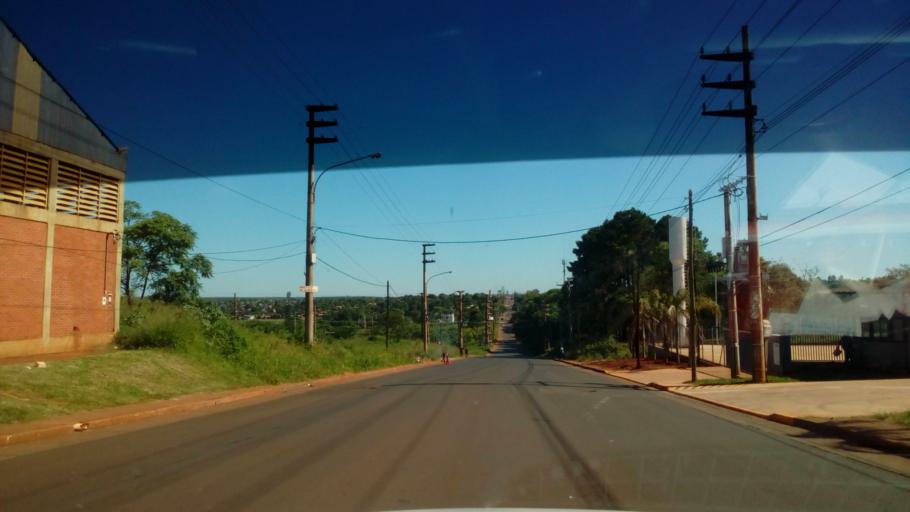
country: AR
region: Misiones
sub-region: Departamento de Capital
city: Posadas
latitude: -27.4163
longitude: -55.9126
